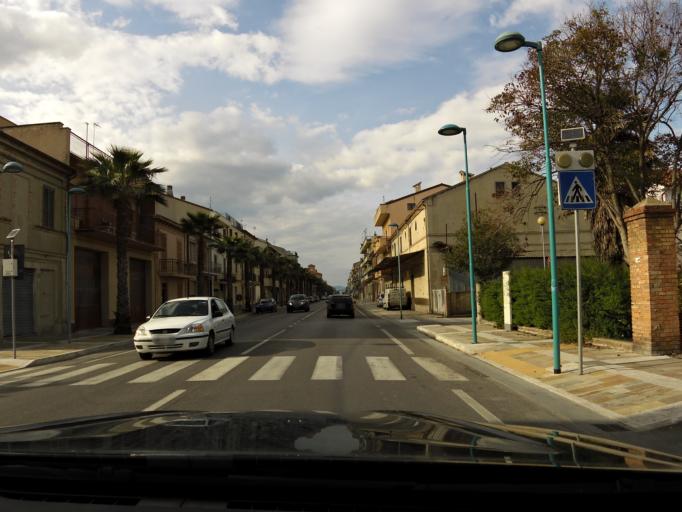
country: IT
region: The Marches
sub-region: Provincia di Macerata
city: Porto Potenza Picena
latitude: 43.3570
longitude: 13.6984
